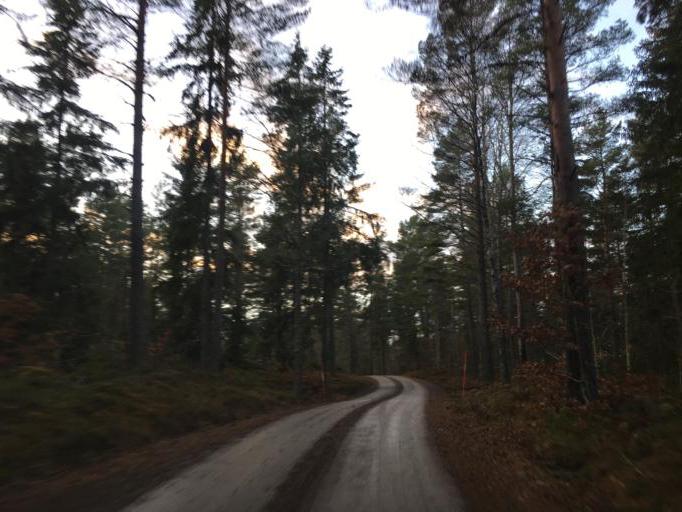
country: SE
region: Kalmar
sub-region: Vasterviks Kommun
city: Vaestervik
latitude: 57.6017
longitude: 16.5265
